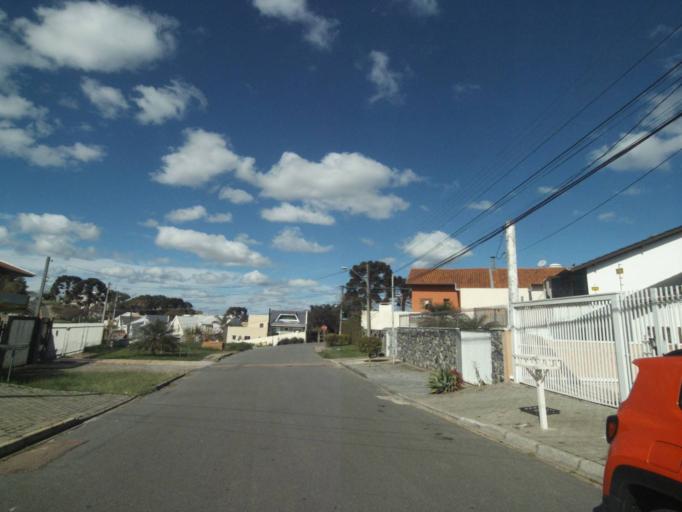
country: BR
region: Parana
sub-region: Curitiba
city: Curitiba
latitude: -25.3871
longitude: -49.2593
